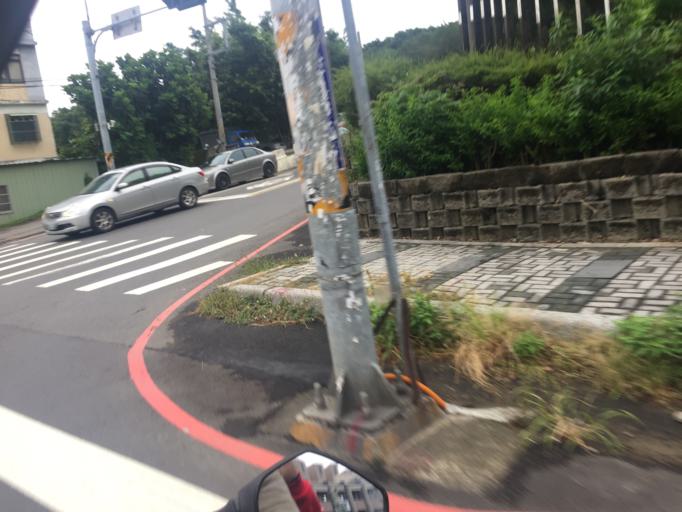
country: TW
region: Taiwan
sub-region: Hsinchu
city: Hsinchu
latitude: 24.7941
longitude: 120.9583
